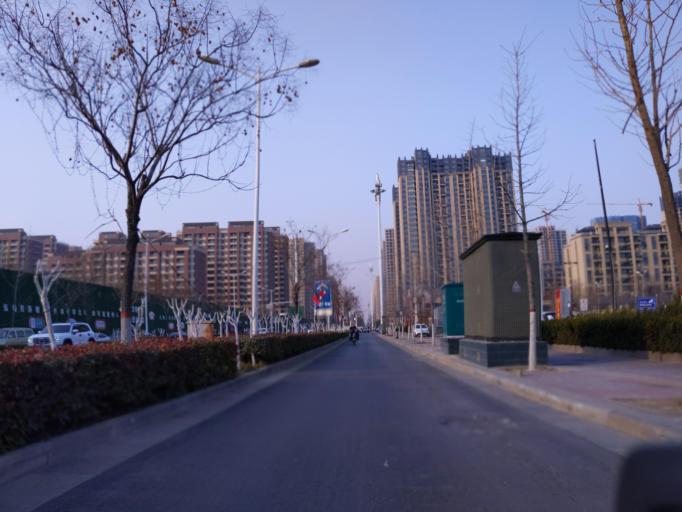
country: CN
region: Henan Sheng
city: Puyang
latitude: 35.7854
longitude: 115.0151
